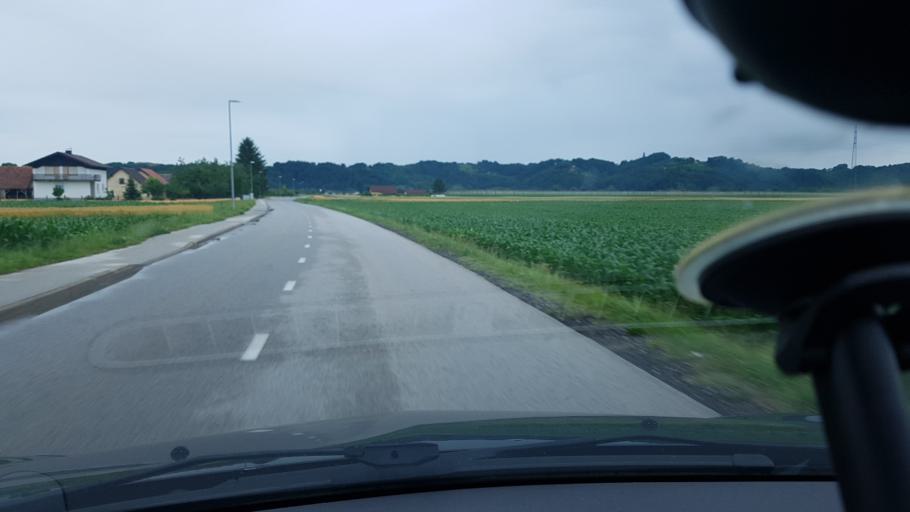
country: SI
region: Videm
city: Videm pri Ptuju
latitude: 46.3796
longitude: 15.8822
